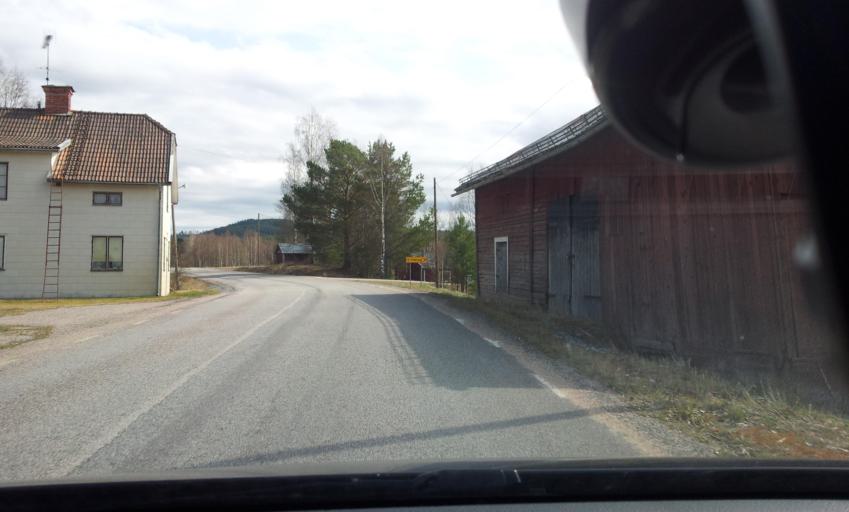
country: SE
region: Gaevleborg
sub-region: Ljusdals Kommun
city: Farila
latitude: 61.7709
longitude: 15.9663
